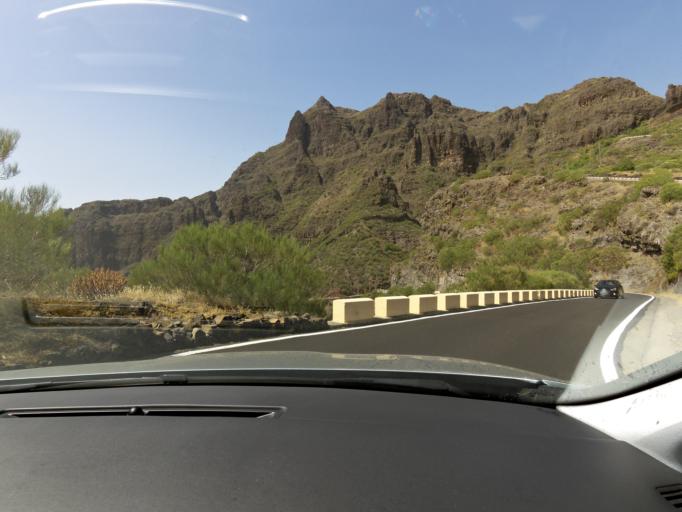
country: ES
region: Canary Islands
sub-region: Provincia de Santa Cruz de Tenerife
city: Santiago del Teide
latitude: 28.2993
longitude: -16.8276
